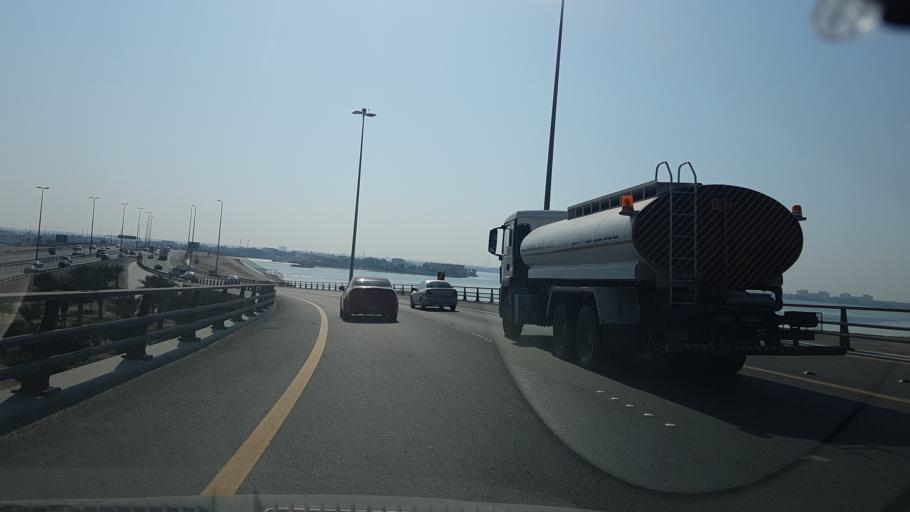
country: BH
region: Manama
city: Manama
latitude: 26.1979
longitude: 50.5901
